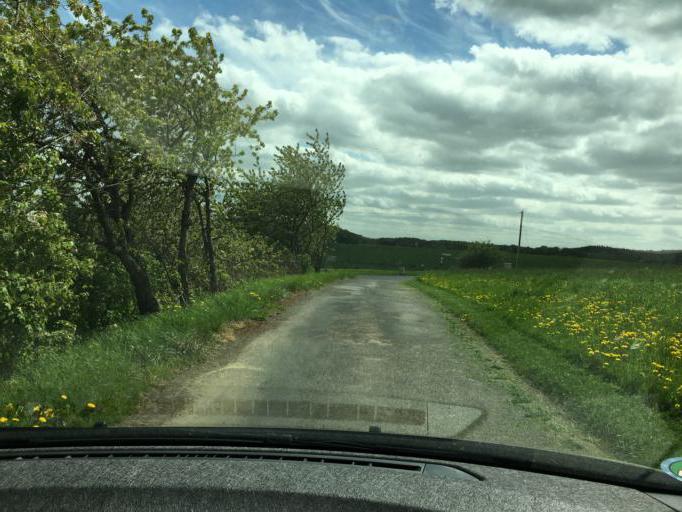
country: DE
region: Rheinland-Pfalz
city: Kirchsahr
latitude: 50.5176
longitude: 6.8753
